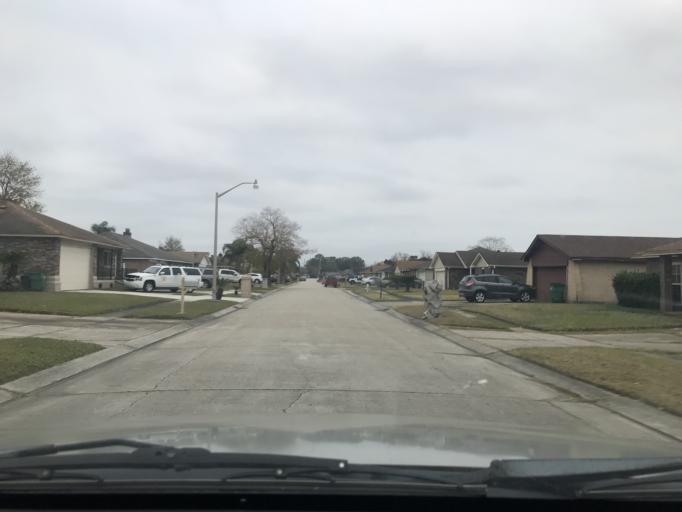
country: US
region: Louisiana
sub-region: Jefferson Parish
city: Woodmere
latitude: 29.8611
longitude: -90.0853
